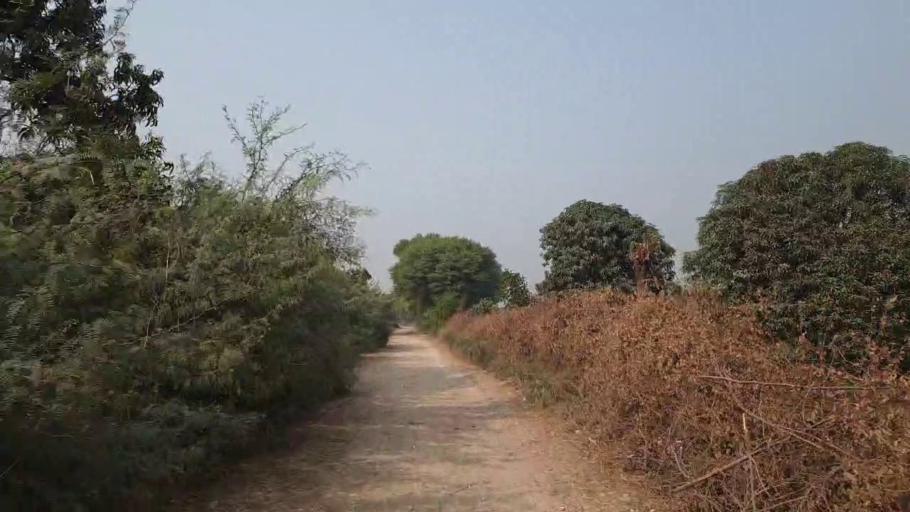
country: PK
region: Sindh
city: Tando Muhammad Khan
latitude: 25.2066
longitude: 68.5609
